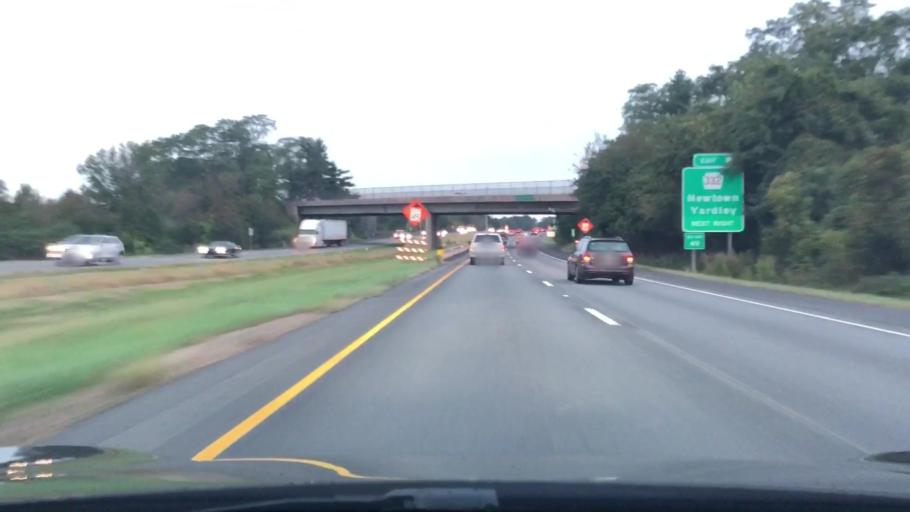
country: US
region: Pennsylvania
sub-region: Bucks County
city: Woodside
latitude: 40.2240
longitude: -74.8811
